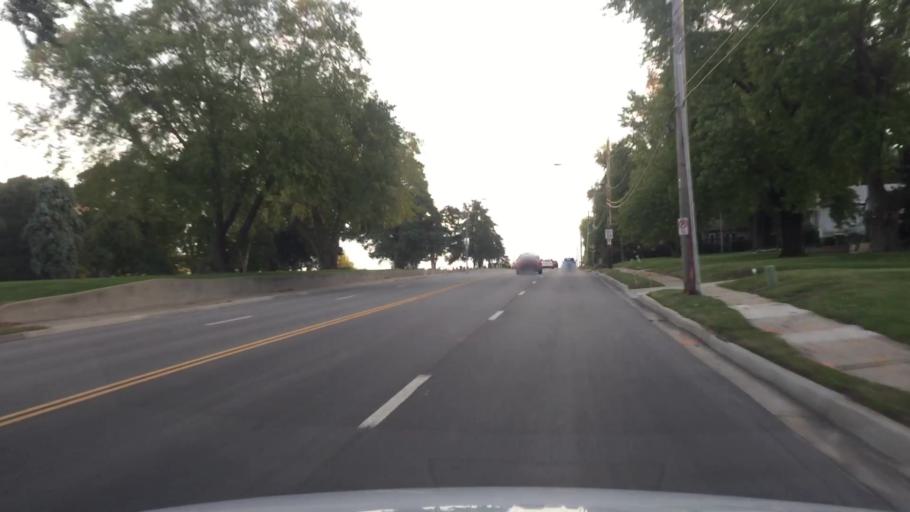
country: US
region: Kansas
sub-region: Johnson County
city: Shawnee
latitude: 39.0202
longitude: -94.7240
